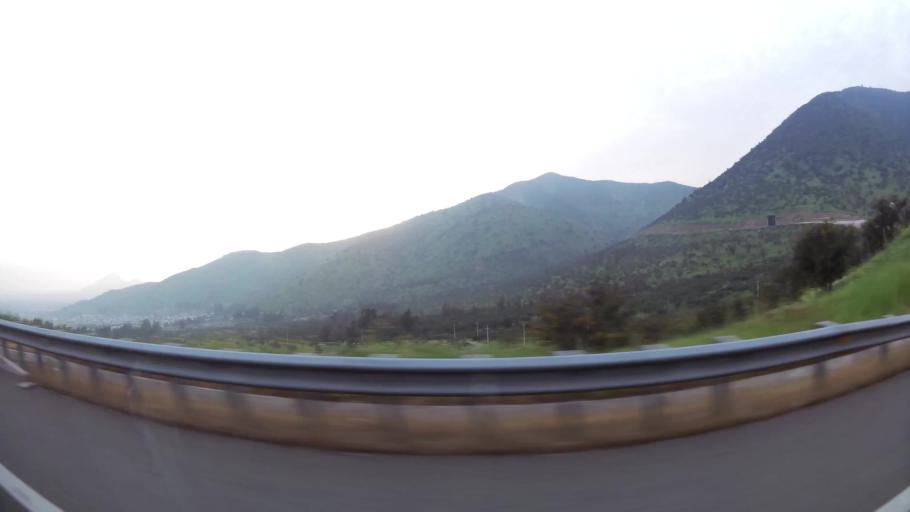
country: CL
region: Santiago Metropolitan
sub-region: Provincia de Chacabuco
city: Chicureo Abajo
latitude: -33.3577
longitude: -70.6156
